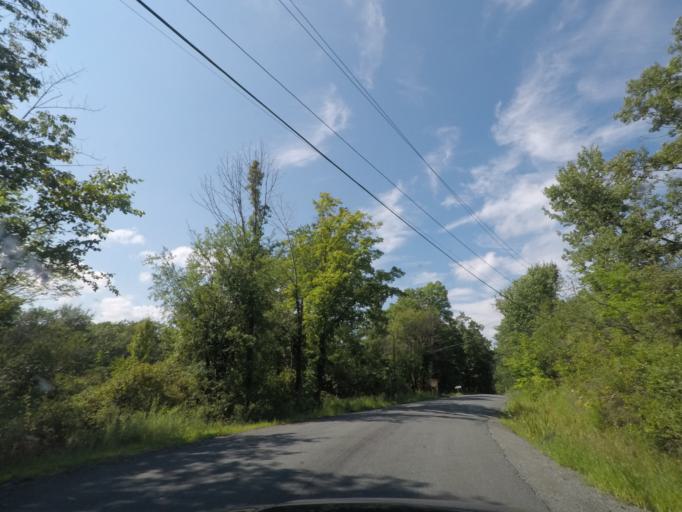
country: US
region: New York
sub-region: Rensselaer County
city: Averill Park
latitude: 42.5930
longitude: -73.5784
